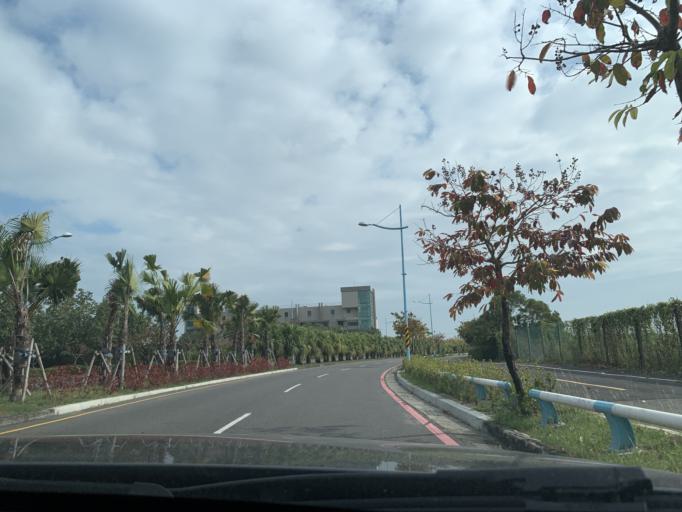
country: TW
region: Taiwan
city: Fengshan
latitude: 22.4534
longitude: 120.4869
